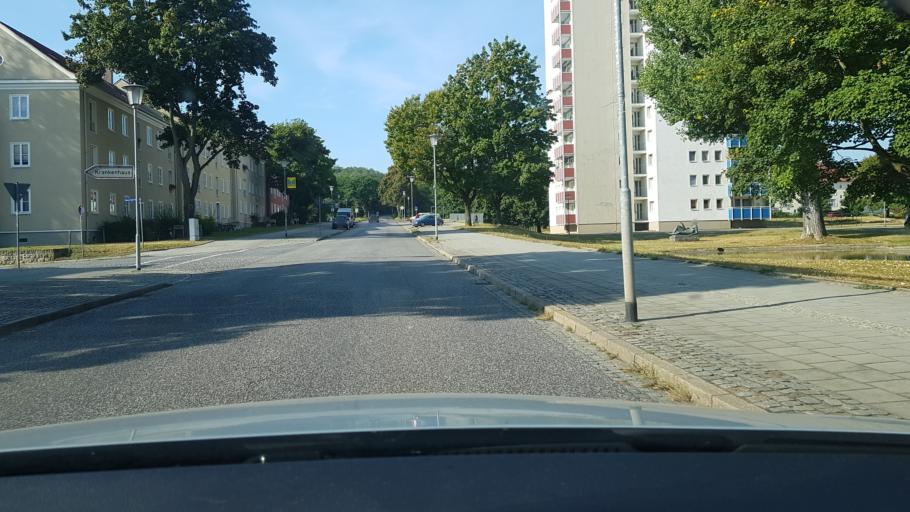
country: DE
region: Brandenburg
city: Eisenhuettenstadt
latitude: 52.1475
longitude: 14.6198
